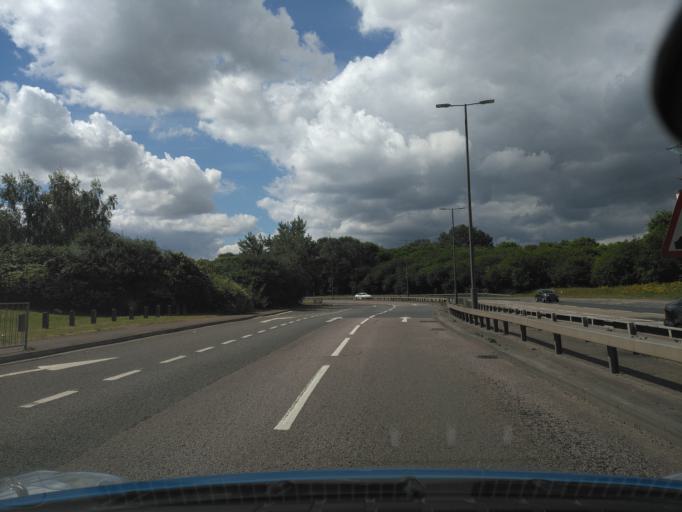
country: GB
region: England
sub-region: Greater London
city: Barking
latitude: 51.5150
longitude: 0.0714
